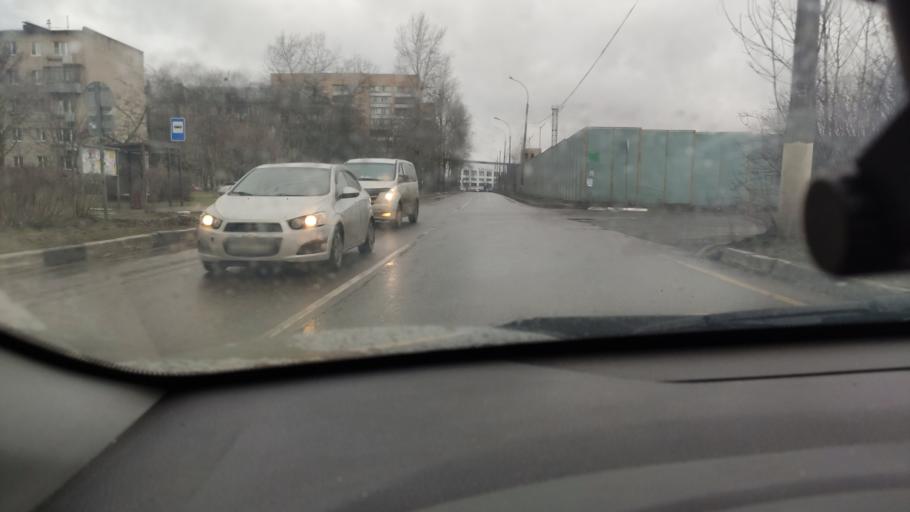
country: RU
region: Moskovskaya
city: Selyatino
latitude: 55.5182
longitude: 36.9824
